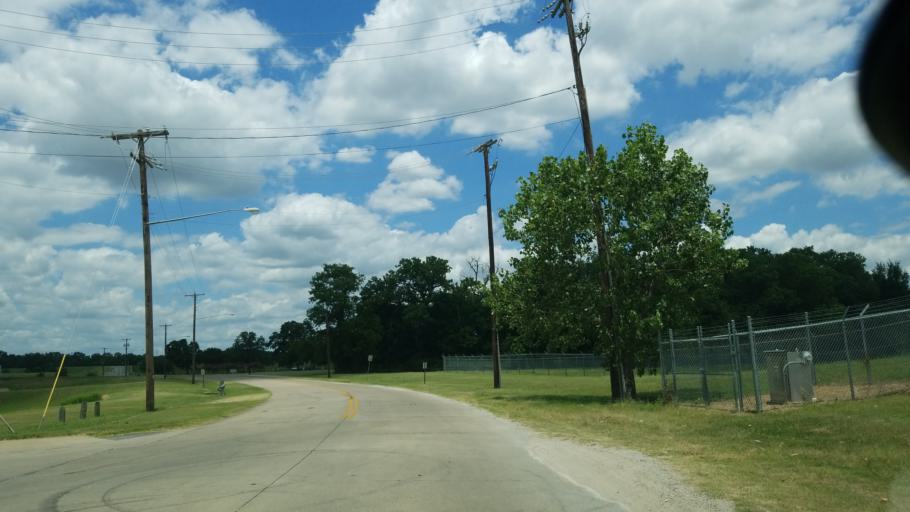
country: US
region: Texas
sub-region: Dallas County
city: Dallas
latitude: 32.7400
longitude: -96.7454
